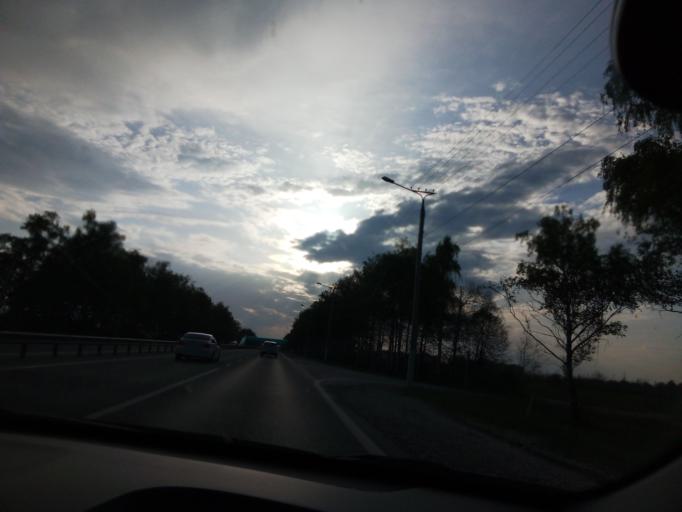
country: RU
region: Chuvashia
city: Novocheboksarsk
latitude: 56.1232
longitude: 47.4079
